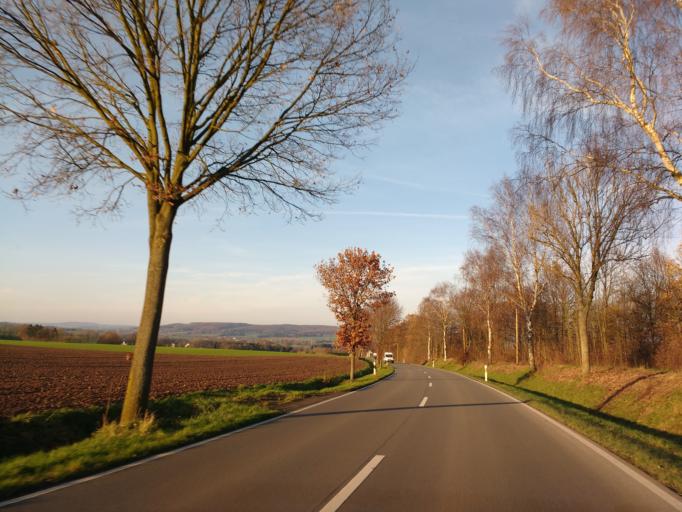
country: DE
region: North Rhine-Westphalia
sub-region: Regierungsbezirk Detmold
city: Blomberg
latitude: 51.9116
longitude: 9.0835
